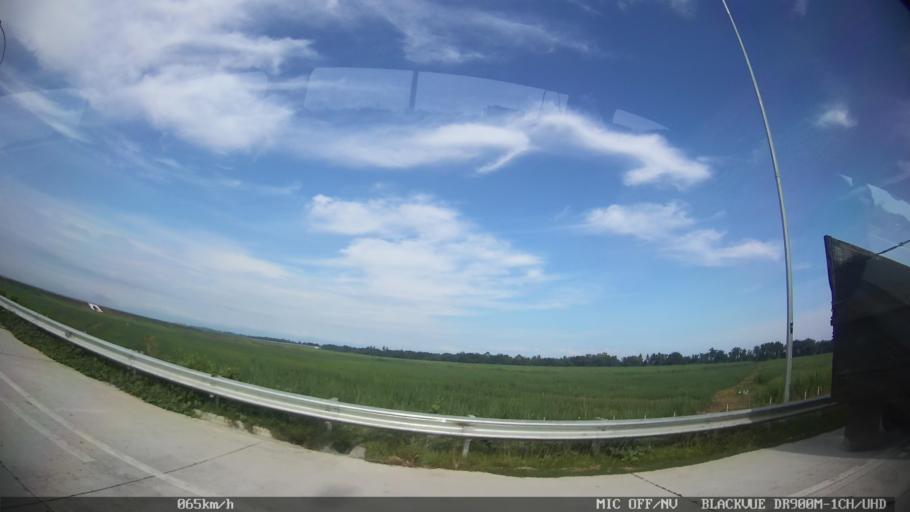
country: ID
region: North Sumatra
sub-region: Kabupaten Langkat
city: Stabat
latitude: 3.7163
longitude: 98.4939
